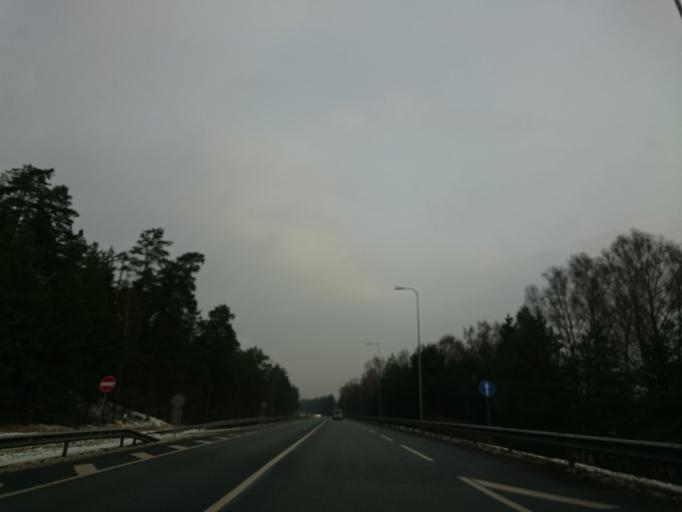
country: LV
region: Carnikava
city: Carnikava
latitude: 57.1501
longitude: 24.3430
